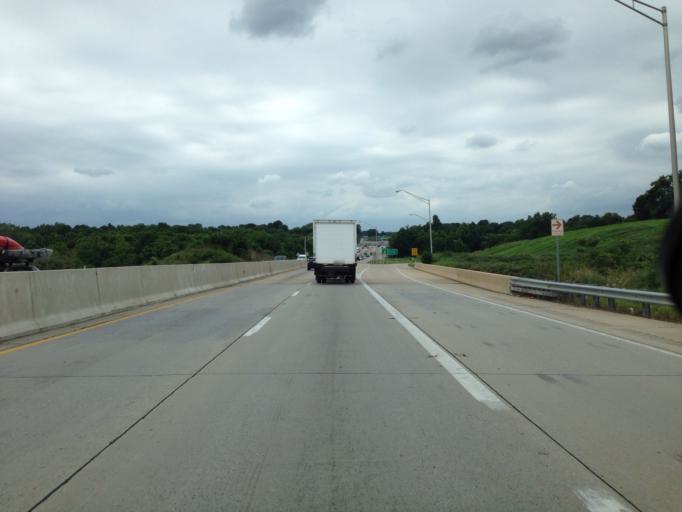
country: US
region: Pennsylvania
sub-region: Lancaster County
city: Lancaster
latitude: 40.0547
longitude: -76.2669
